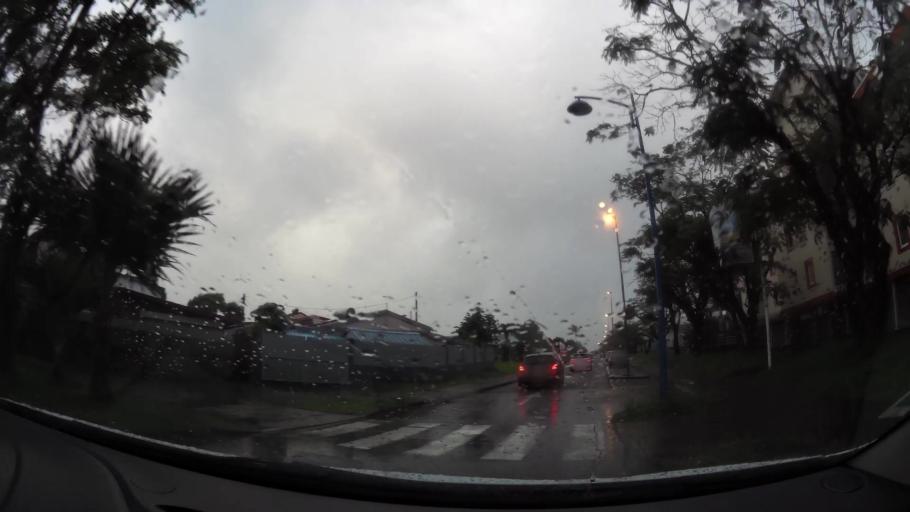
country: RE
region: Reunion
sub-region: Reunion
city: Saint-Benoit
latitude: -21.0397
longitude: 55.7162
